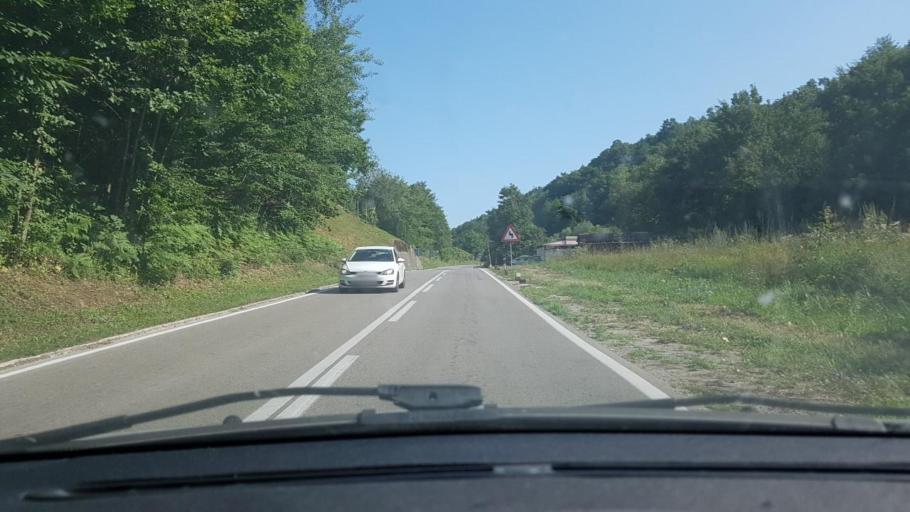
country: BA
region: Federation of Bosnia and Herzegovina
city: Skokovi
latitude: 45.0141
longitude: 15.9035
